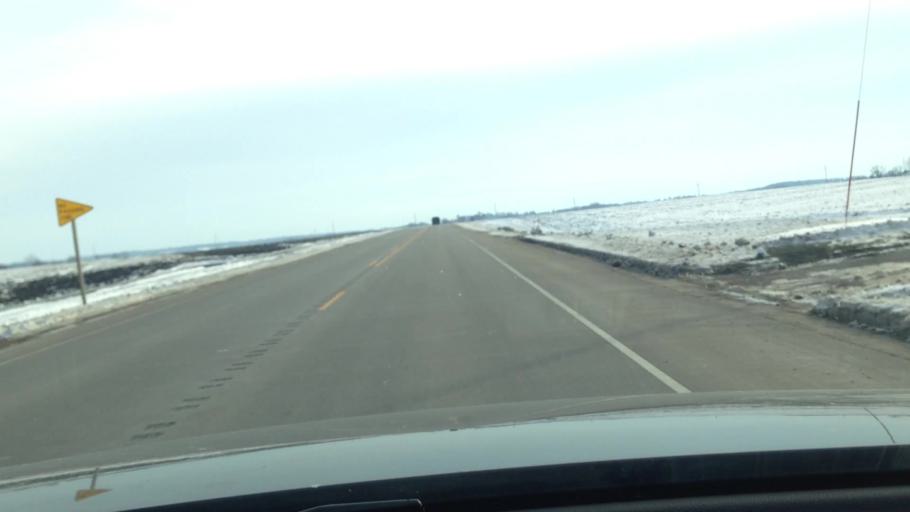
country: US
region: Illinois
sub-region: McHenry County
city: Hebron
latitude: 42.5231
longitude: -88.4428
